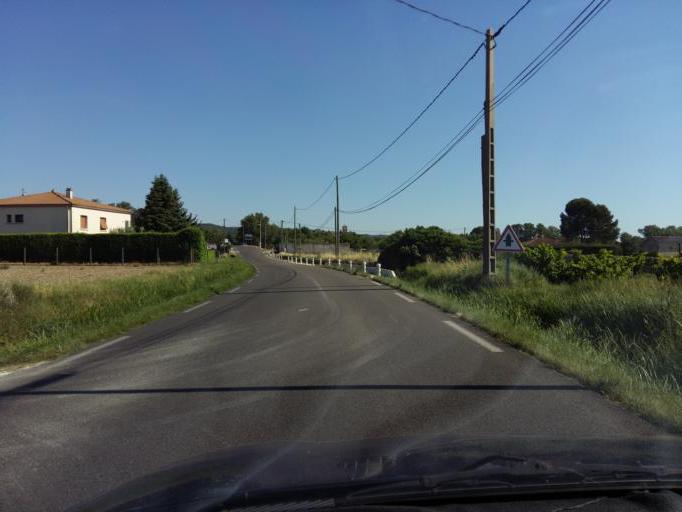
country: FR
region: Provence-Alpes-Cote d'Azur
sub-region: Departement du Vaucluse
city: Valreas
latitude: 44.3932
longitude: 4.9879
